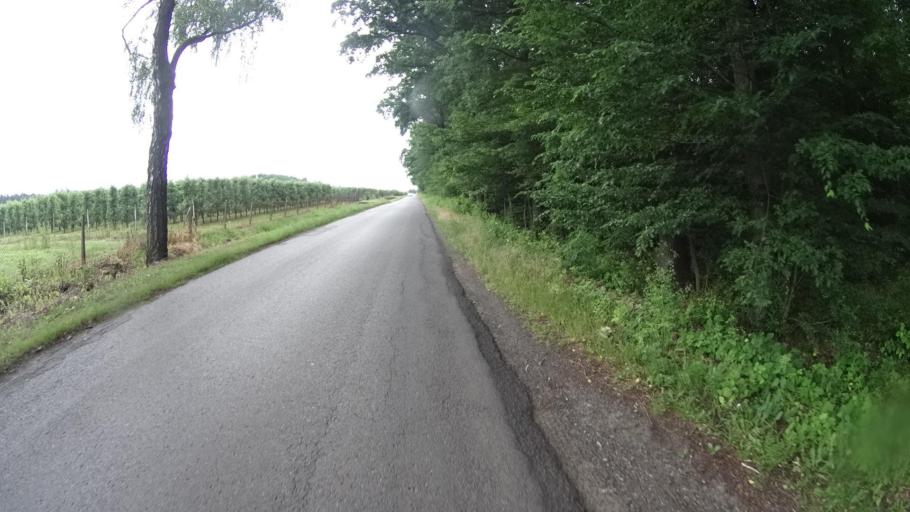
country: PL
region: Masovian Voivodeship
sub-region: Powiat grojecki
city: Goszczyn
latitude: 51.7799
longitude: 20.8537
